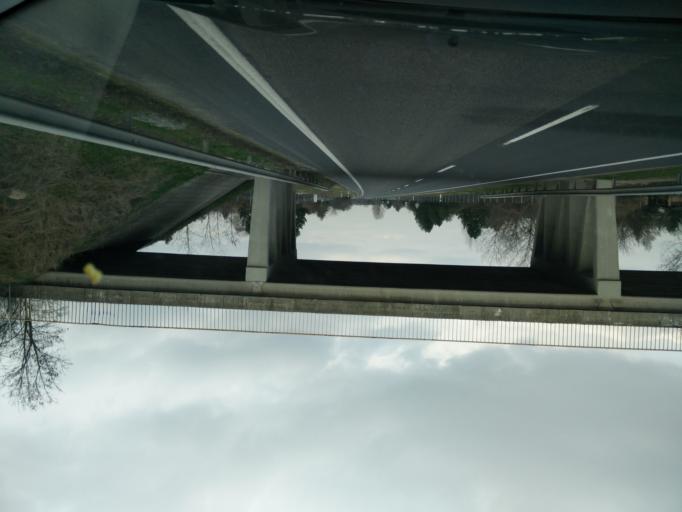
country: HU
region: Gyor-Moson-Sopron
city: Gyor
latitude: 47.7162
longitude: 17.7160
